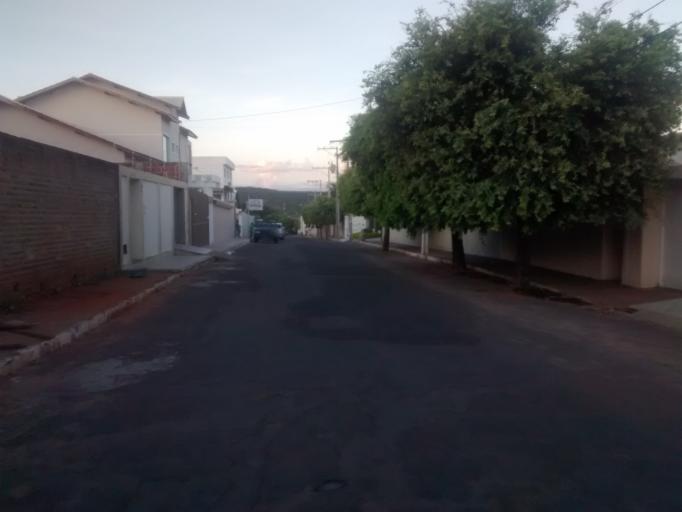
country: BR
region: Bahia
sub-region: Brumado
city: Brumado
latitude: -14.2046
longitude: -41.6769
